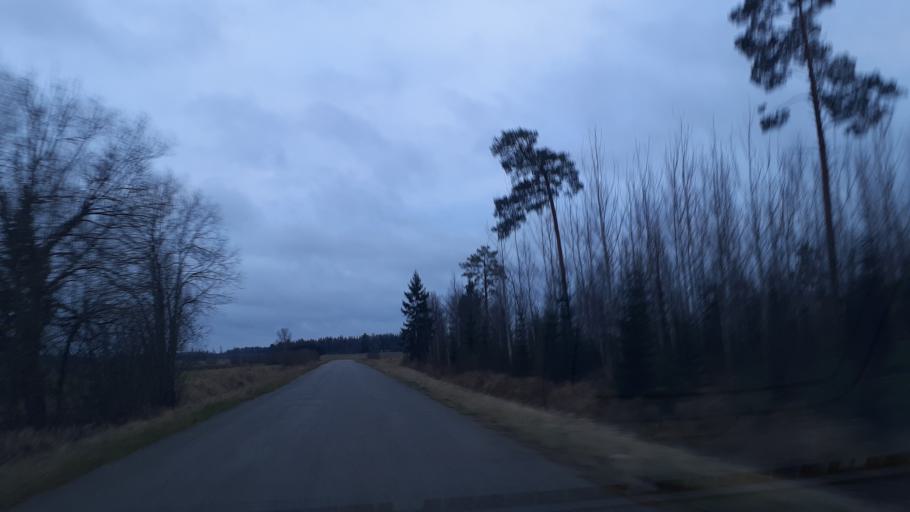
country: LV
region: Kuldigas Rajons
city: Kuldiga
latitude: 57.0324
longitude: 22.1571
